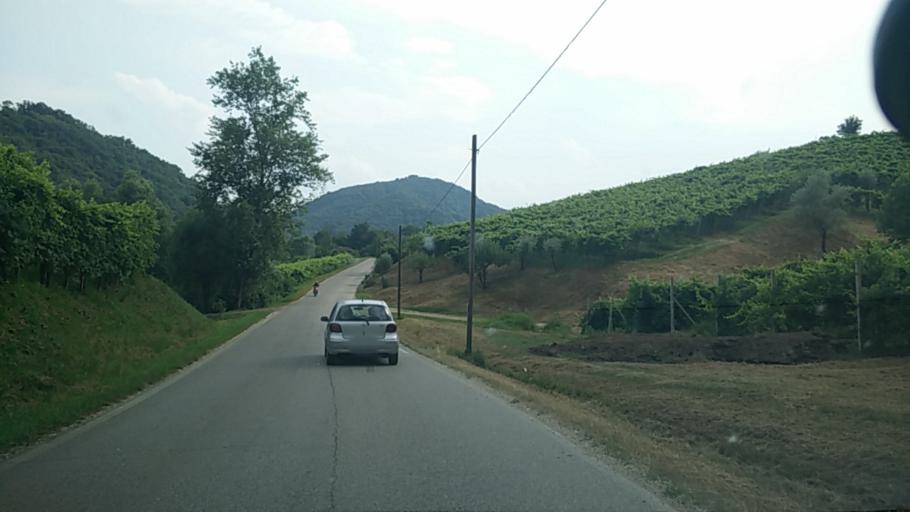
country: IT
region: Veneto
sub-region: Provincia di Treviso
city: Miane
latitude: 45.9169
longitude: 12.0796
